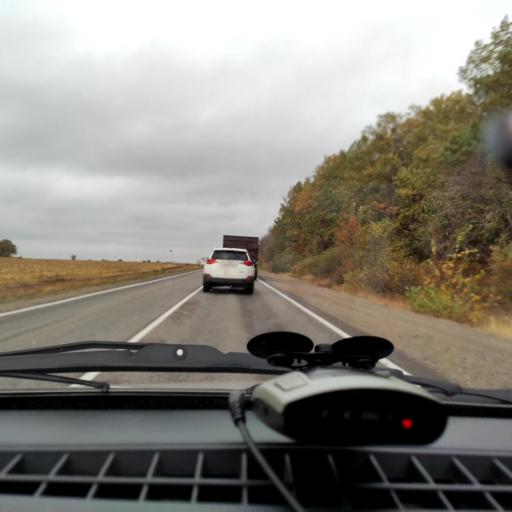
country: RU
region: Voronezj
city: Kolodeznyy
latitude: 51.3832
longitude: 39.0106
